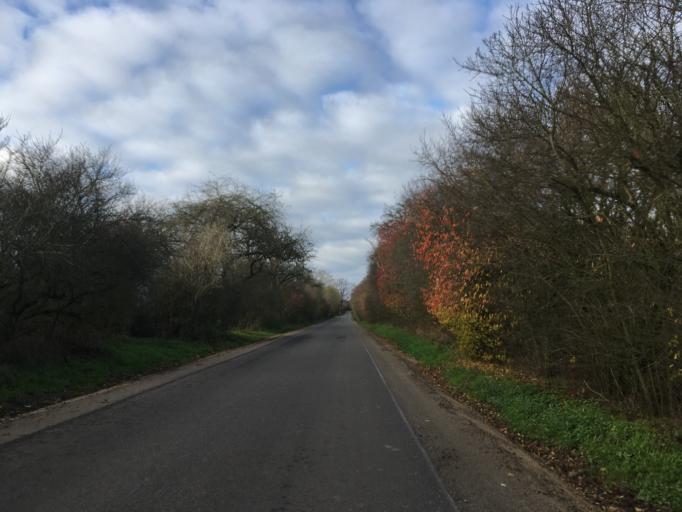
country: DE
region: Brandenburg
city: Waldsieversdorf
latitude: 52.5473
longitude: 14.0274
